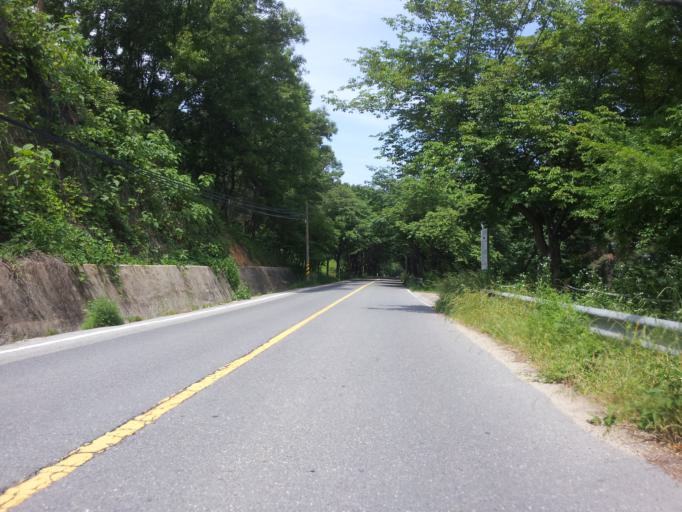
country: KR
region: Daejeon
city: Sintansin
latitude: 36.4325
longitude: 127.4684
